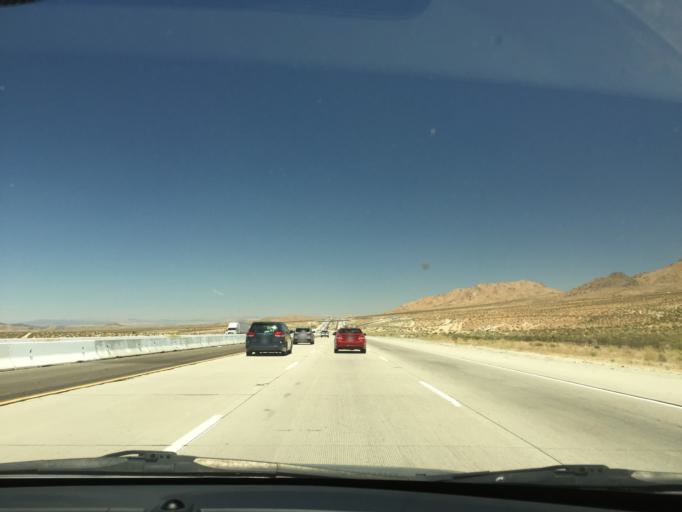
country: US
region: California
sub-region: San Bernardino County
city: Victorville
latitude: 34.6915
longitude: -117.2105
